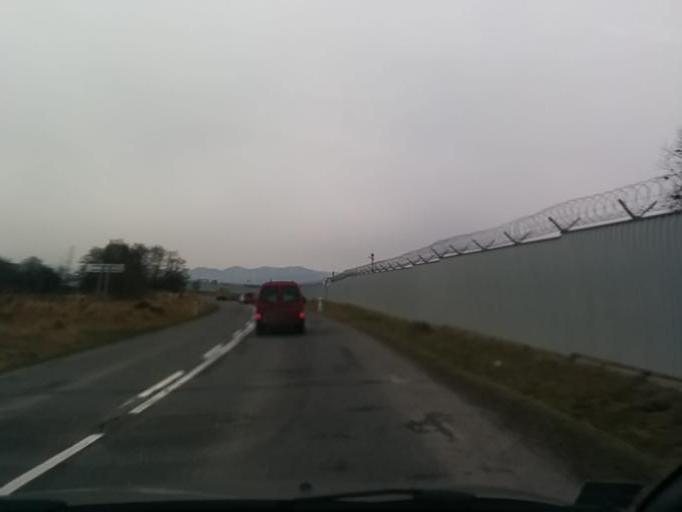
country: SK
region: Banskobystricky
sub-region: Okres Banska Bystrica
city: Zvolen
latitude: 48.6327
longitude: 19.1398
